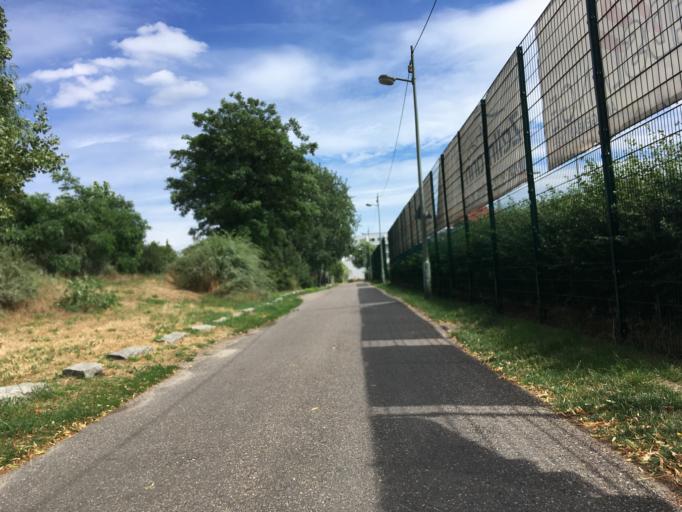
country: DE
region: Berlin
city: Altglienicke
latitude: 52.4198
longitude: 13.5344
